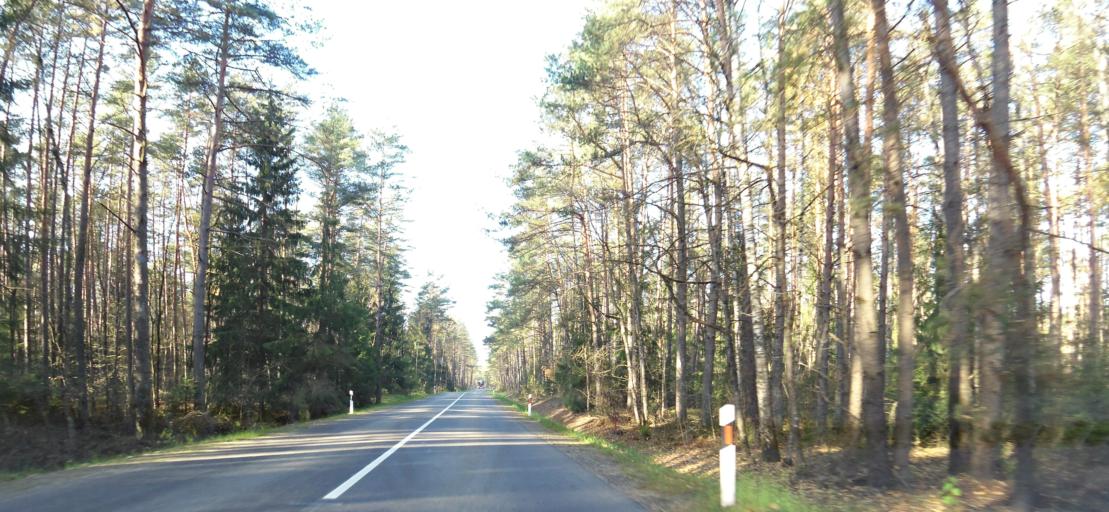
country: LT
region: Vilnius County
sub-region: Trakai
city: Rudiskes
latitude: 54.5106
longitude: 24.9269
